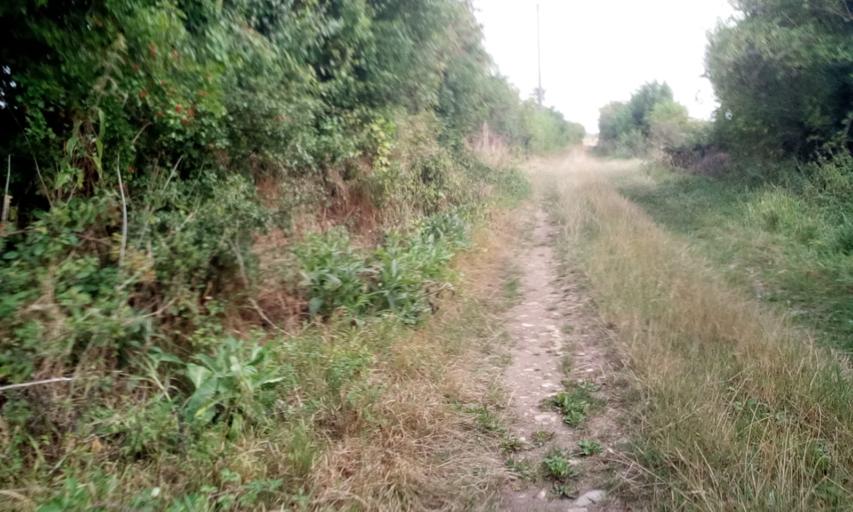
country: FR
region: Lower Normandy
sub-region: Departement du Calvados
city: Bellengreville
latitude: 49.1331
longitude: -0.2212
